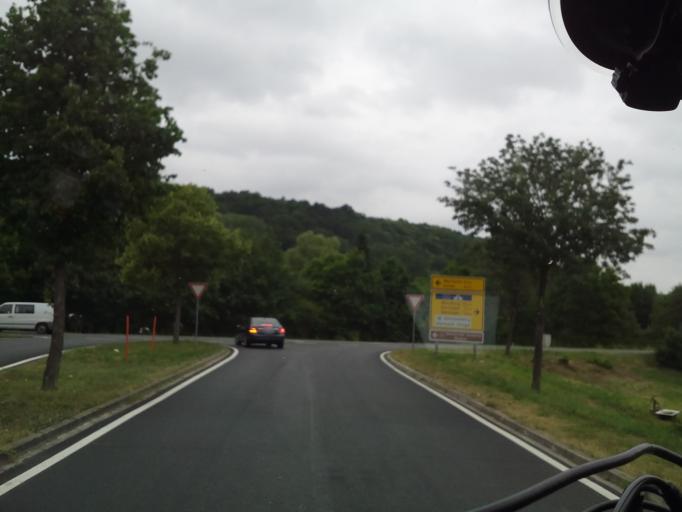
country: DE
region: Bavaria
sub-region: Regierungsbezirk Unterfranken
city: Kreuzwertheim
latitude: 49.7502
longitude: 9.5715
